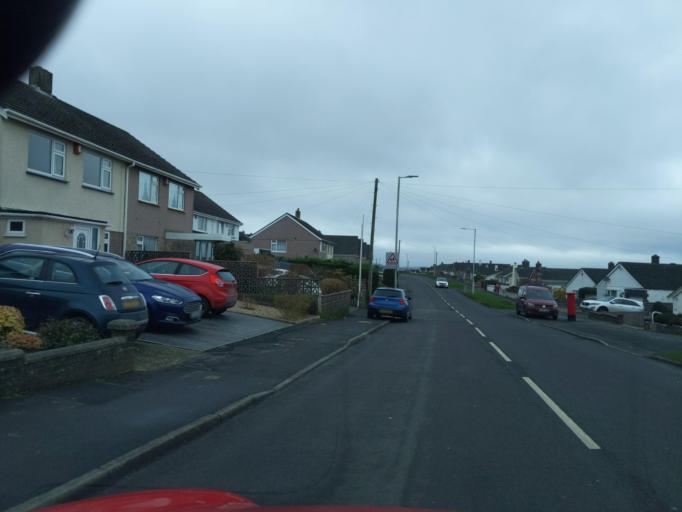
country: GB
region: England
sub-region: Plymouth
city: Plymstock
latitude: 50.3617
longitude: -4.0768
